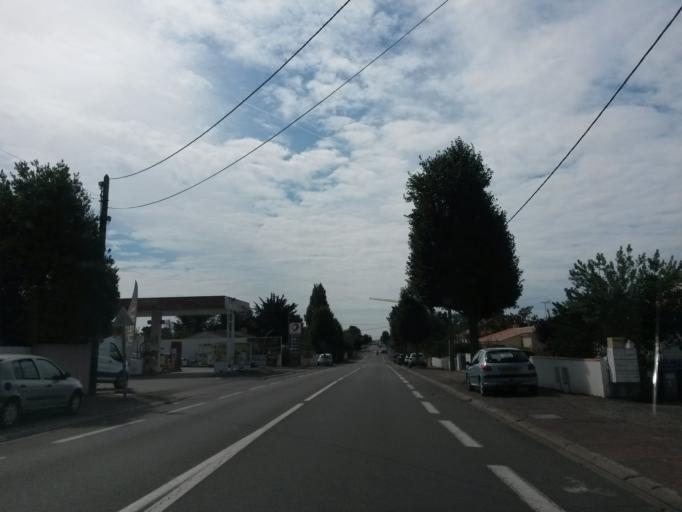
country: FR
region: Pays de la Loire
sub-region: Departement de la Vendee
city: Olonne-sur-Mer
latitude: 46.5183
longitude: -1.7759
